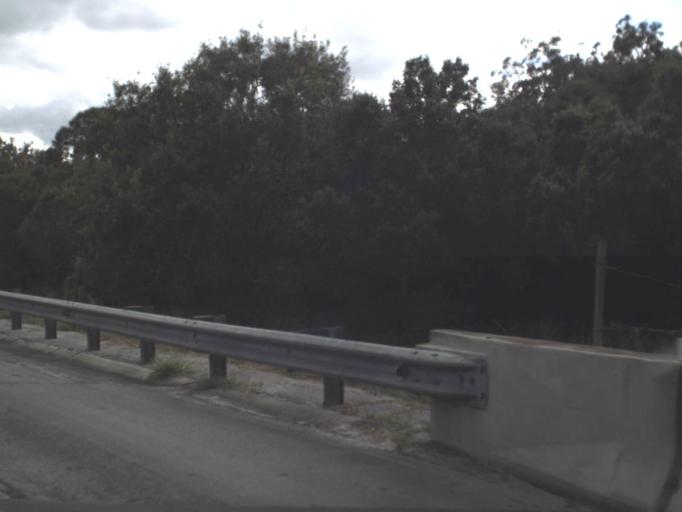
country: US
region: Florida
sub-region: Saint Lucie County
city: Fort Pierce South
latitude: 27.4025
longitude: -80.3979
